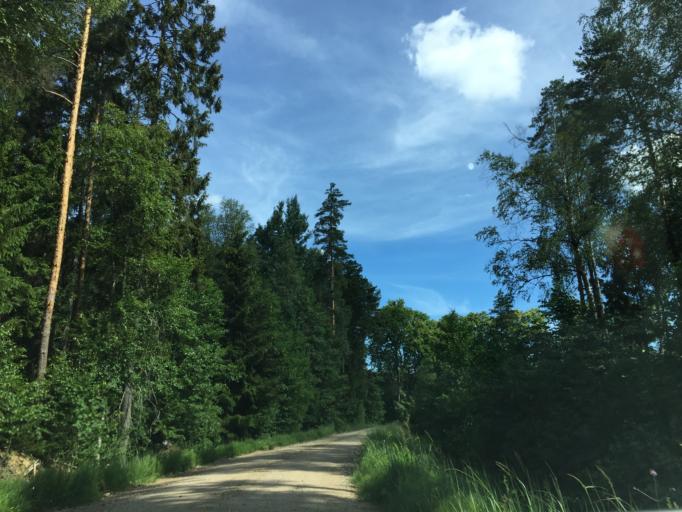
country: LV
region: Dundaga
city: Dundaga
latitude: 57.4262
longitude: 22.0743
